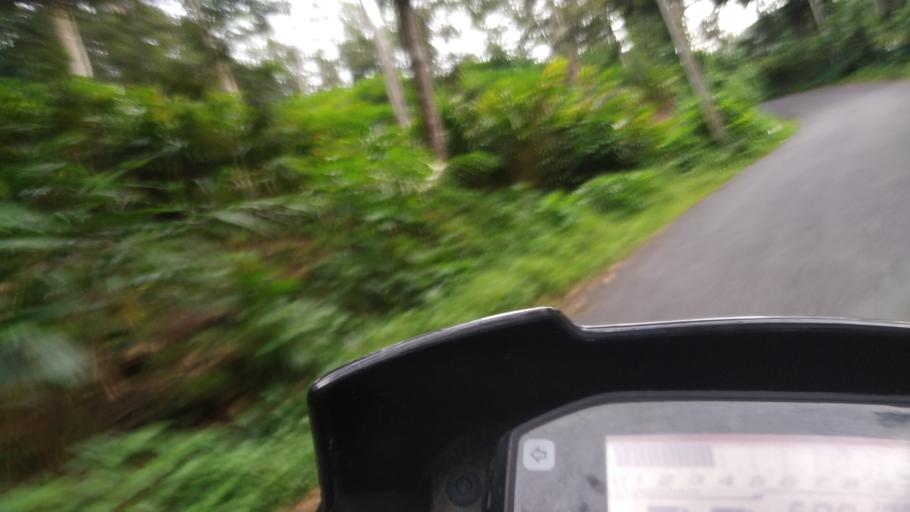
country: IN
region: Tamil Nadu
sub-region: Theni
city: Bodinayakkanur
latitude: 10.0324
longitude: 77.2301
